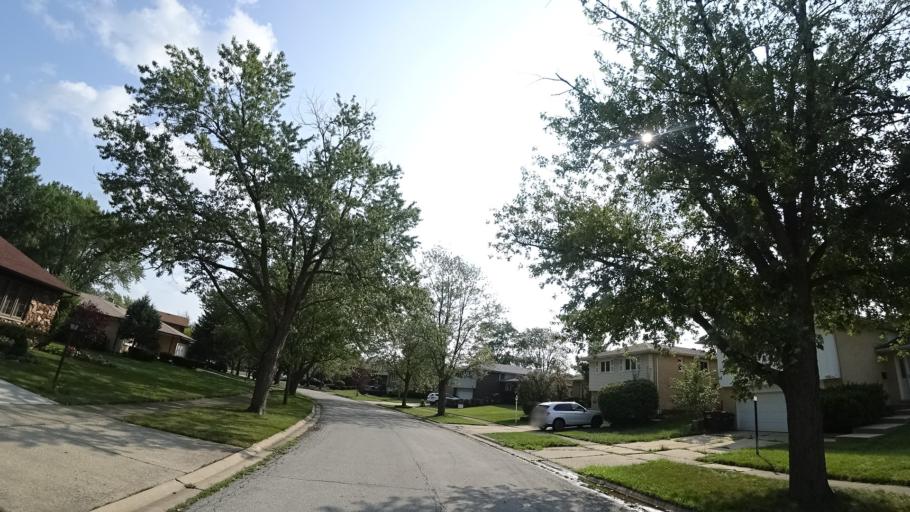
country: US
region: Illinois
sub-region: Cook County
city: Oak Forest
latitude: 41.6130
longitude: -87.7812
